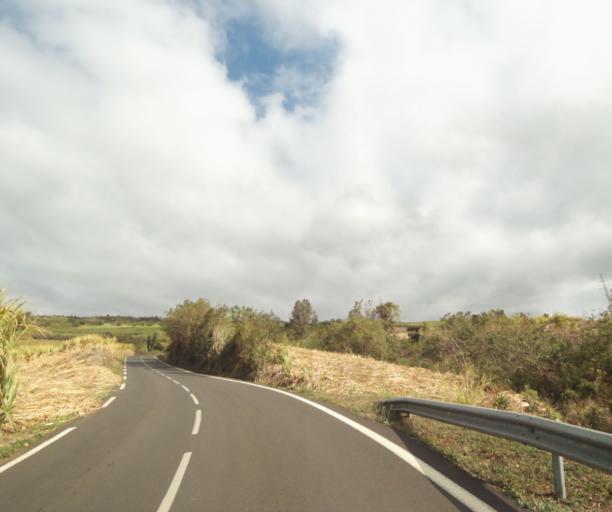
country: RE
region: Reunion
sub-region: Reunion
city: Saint-Paul
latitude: -21.0230
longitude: 55.3118
